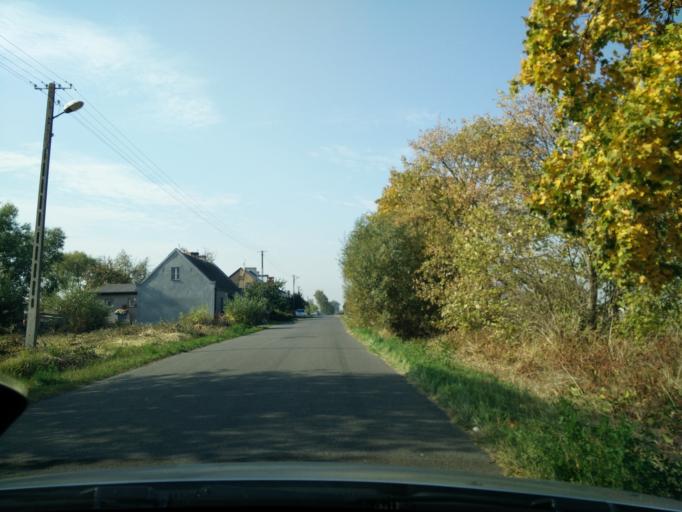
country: PL
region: Greater Poland Voivodeship
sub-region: Powiat sredzki
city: Dominowo
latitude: 52.3172
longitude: 17.3272
